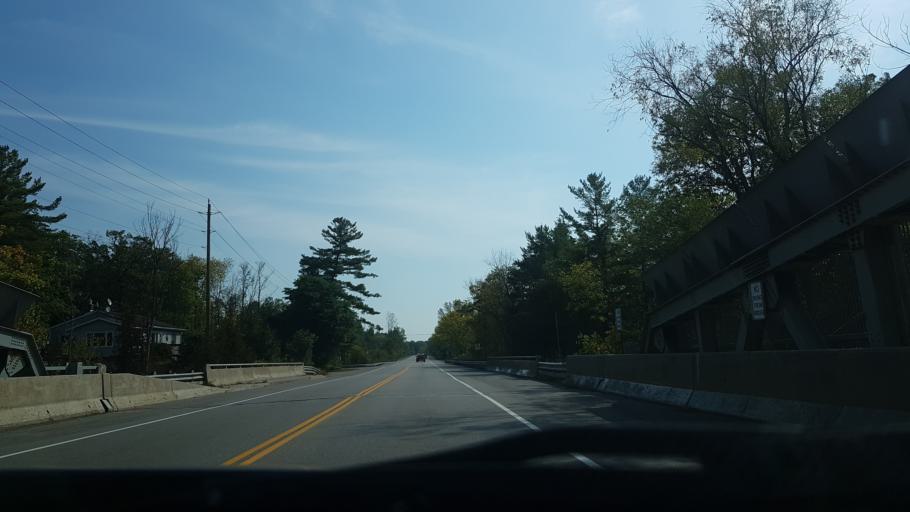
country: CA
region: Ontario
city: Orillia
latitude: 44.7465
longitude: -79.3248
